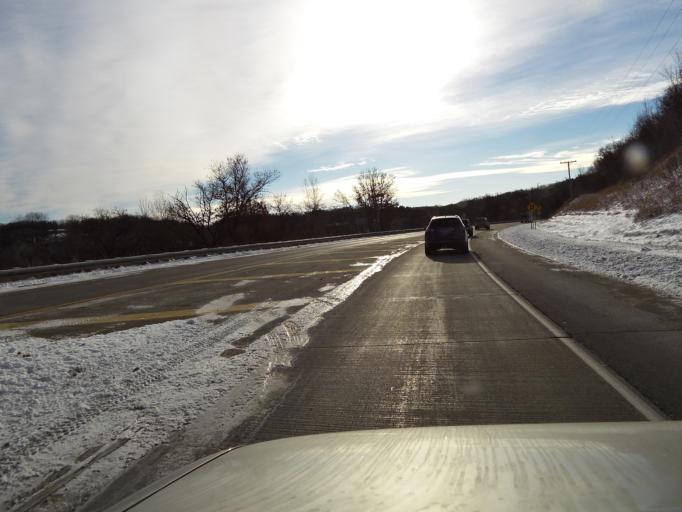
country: US
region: Minnesota
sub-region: Dakota County
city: Inver Grove Heights
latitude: 44.8285
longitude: -93.0847
